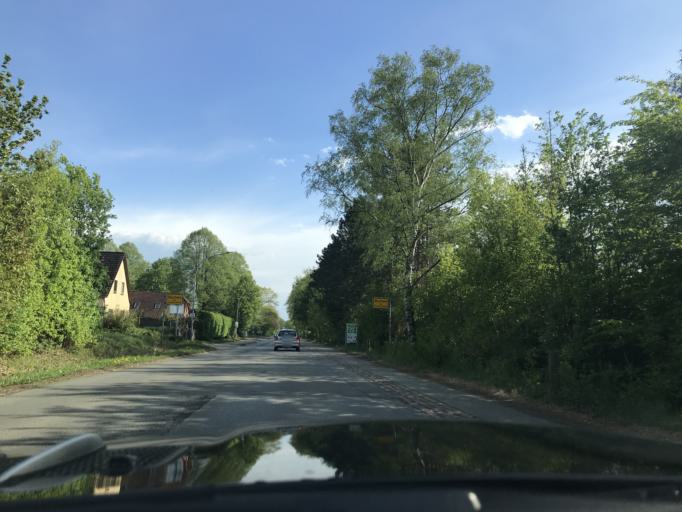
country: DE
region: Schleswig-Holstein
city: Buchen
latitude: 53.4943
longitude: 10.6134
